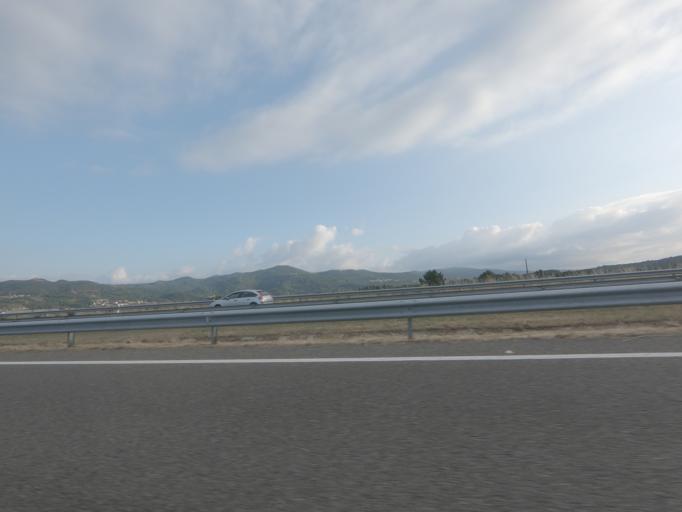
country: ES
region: Galicia
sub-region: Provincia de Ourense
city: Allariz
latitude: 42.2048
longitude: -7.8017
